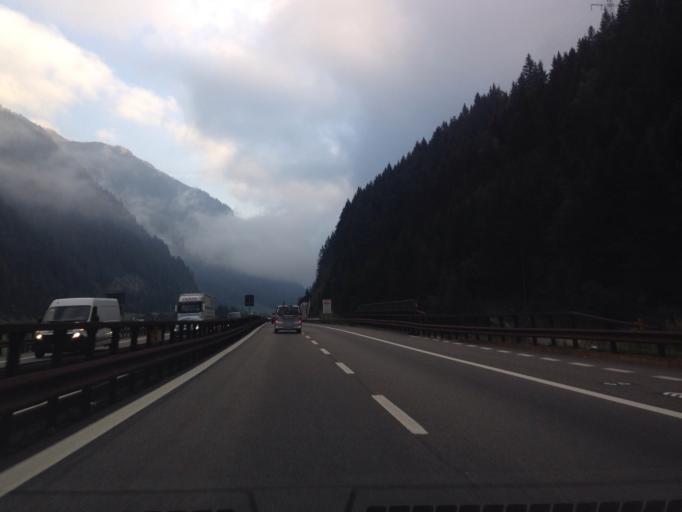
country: IT
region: Trentino-Alto Adige
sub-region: Bolzano
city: Colle Isarco
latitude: 46.9657
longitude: 11.4672
